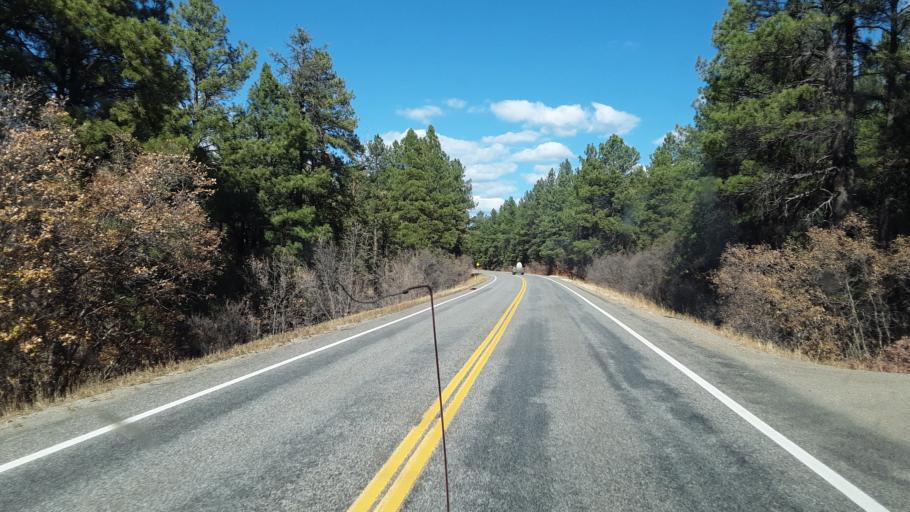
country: US
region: Colorado
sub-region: La Plata County
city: Bayfield
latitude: 37.2166
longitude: -107.3394
